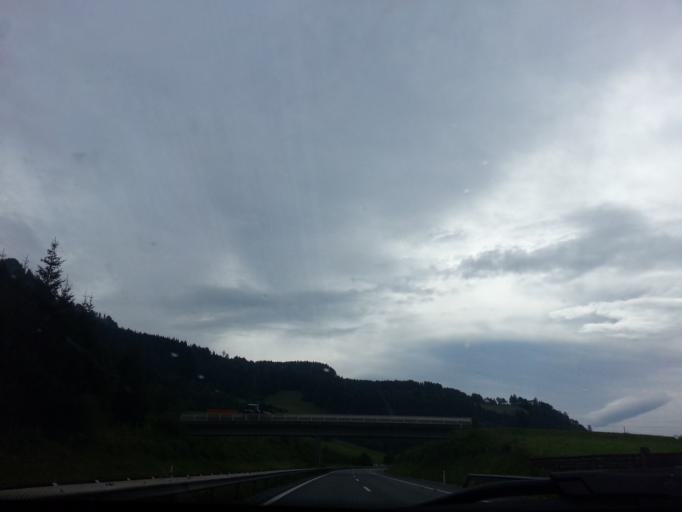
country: AT
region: Styria
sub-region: Politischer Bezirk Leoben
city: Wald am Schoberpass
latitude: 47.4676
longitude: 14.6431
